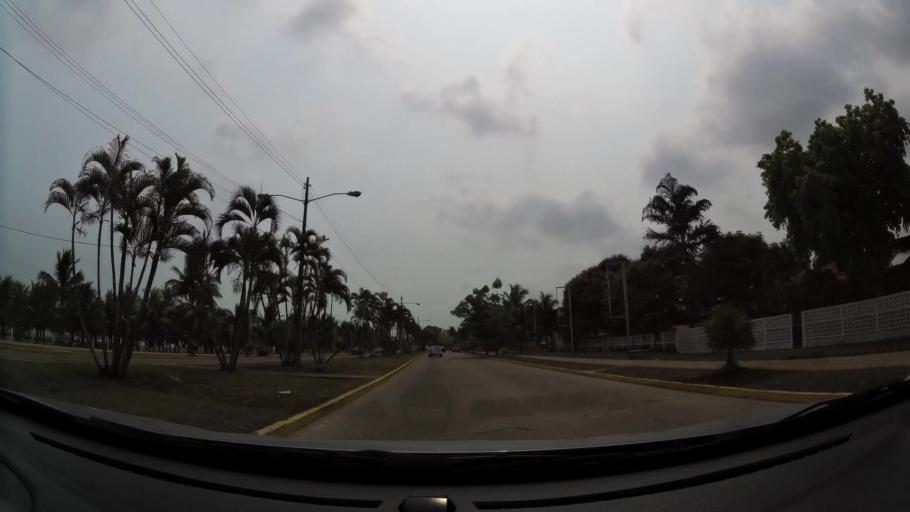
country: HN
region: Atlantida
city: Tela
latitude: 15.7814
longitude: -87.4576
